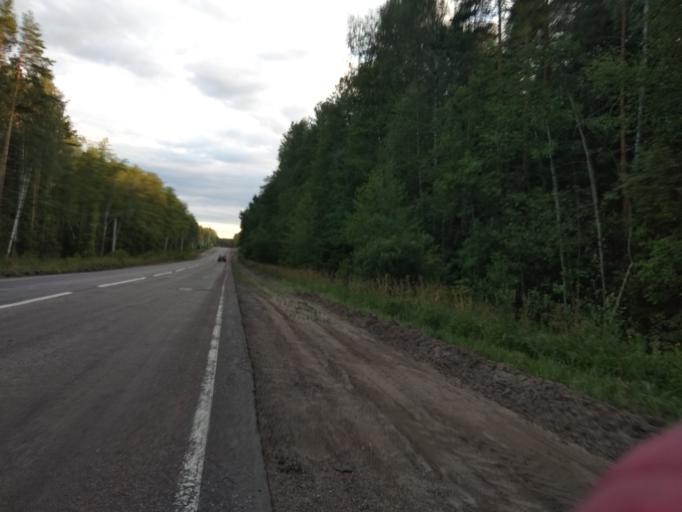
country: RU
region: Moskovskaya
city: Misheronskiy
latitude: 55.6370
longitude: 39.7495
